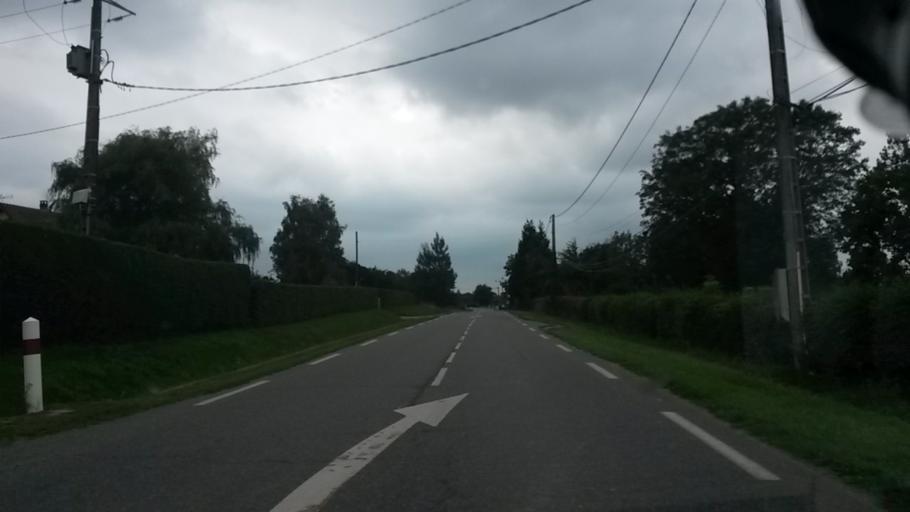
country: FR
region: Haute-Normandie
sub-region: Departement de la Seine-Maritime
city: Gaillefontaine
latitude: 49.7015
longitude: 1.6498
